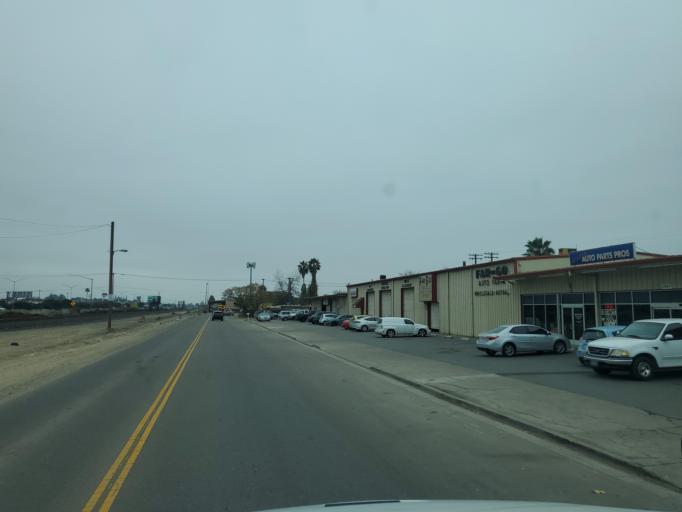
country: US
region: California
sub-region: Stanislaus County
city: Bystrom
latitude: 37.6080
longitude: -120.9767
